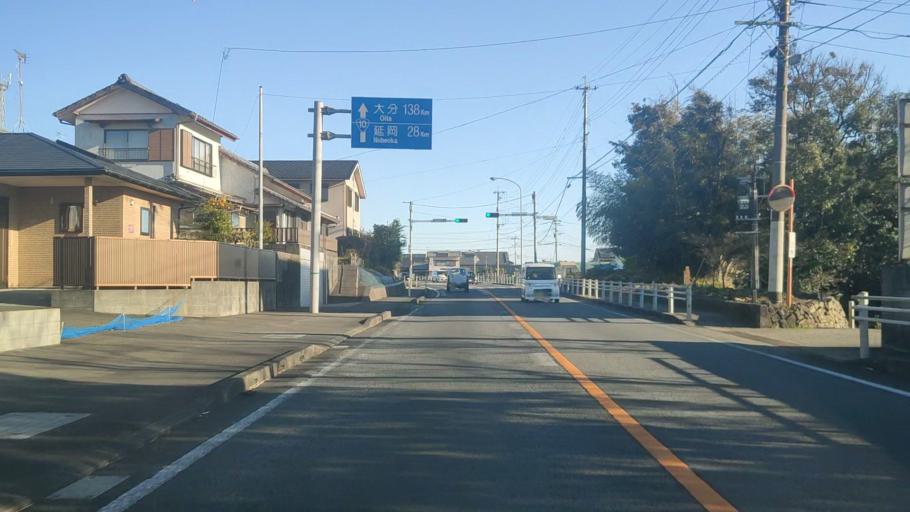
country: JP
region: Miyazaki
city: Nobeoka
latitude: 32.3712
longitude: 131.6300
